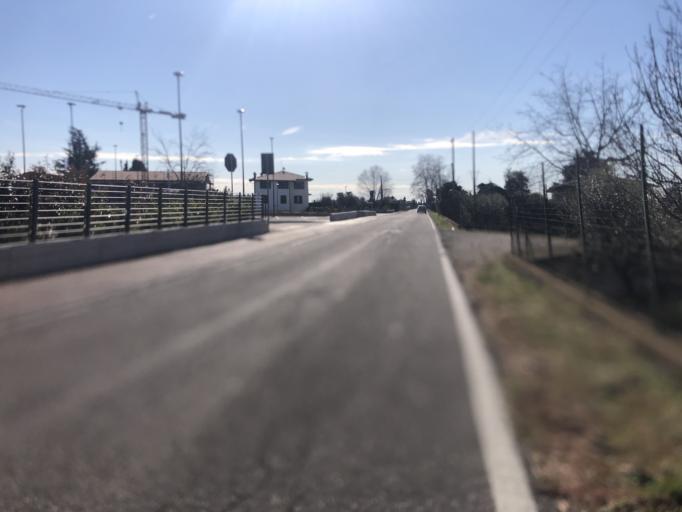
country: IT
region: Veneto
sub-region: Provincia di Verona
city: Ospedaletto
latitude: 45.5031
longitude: 10.8364
